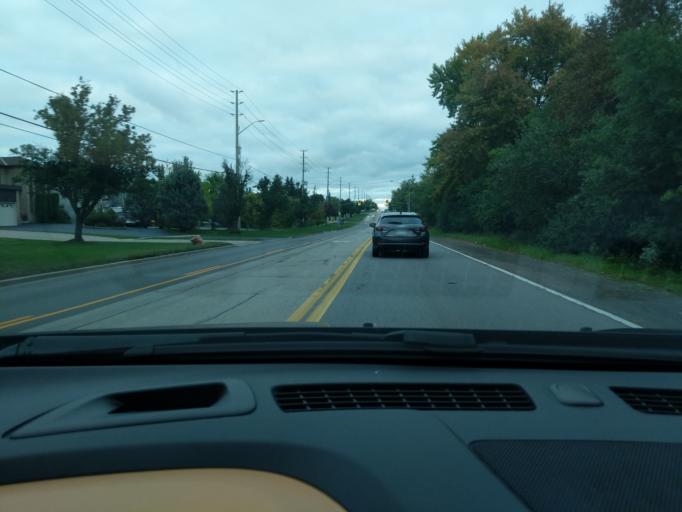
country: CA
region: Ontario
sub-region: York
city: Richmond Hill
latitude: 43.8852
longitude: -79.4621
